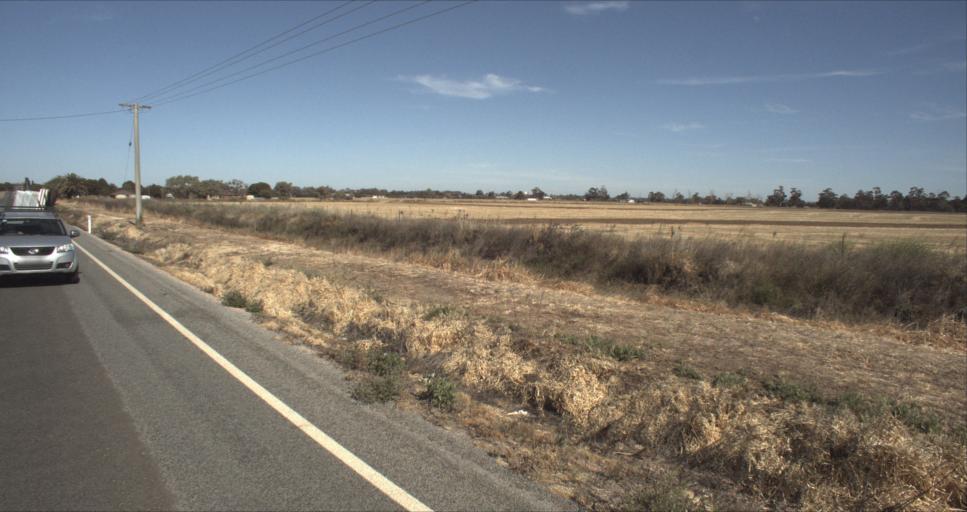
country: AU
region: New South Wales
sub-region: Leeton
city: Leeton
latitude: -34.5608
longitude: 146.4368
